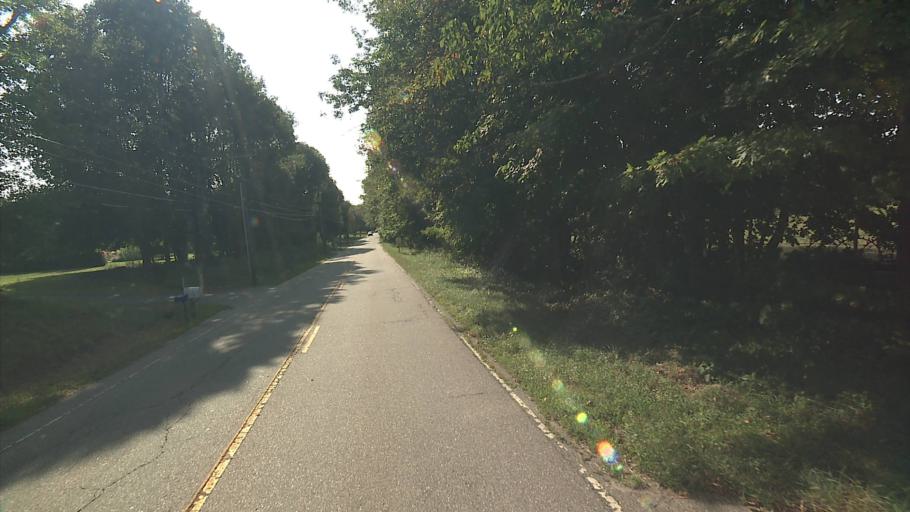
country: US
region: Connecticut
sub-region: Windham County
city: Willimantic
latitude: 41.6626
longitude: -72.2524
